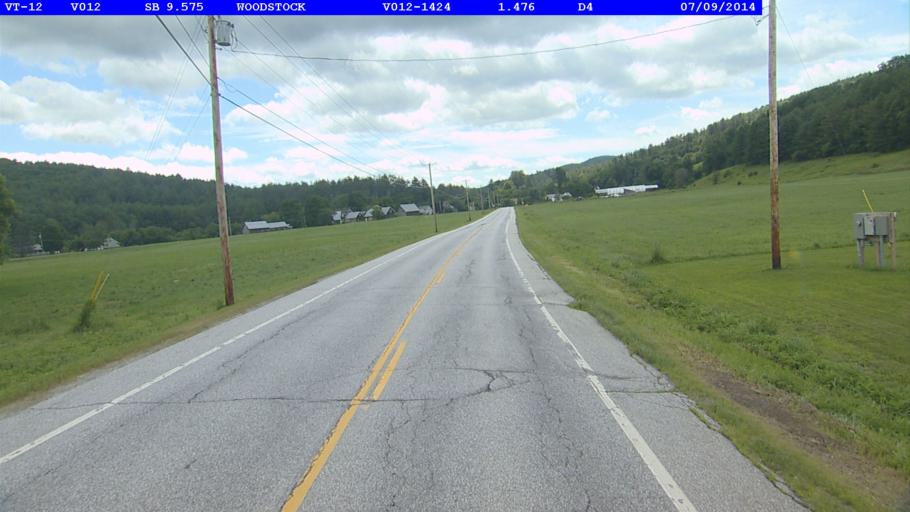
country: US
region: Vermont
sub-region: Windsor County
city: Woodstock
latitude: 43.6420
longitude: -72.5292
